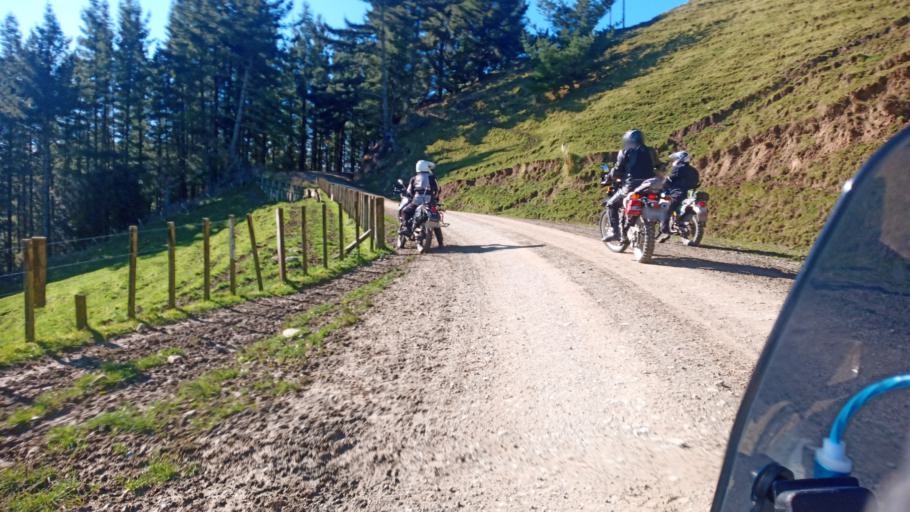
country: NZ
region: Gisborne
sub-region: Gisborne District
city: Gisborne
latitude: -38.2869
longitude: 177.8579
